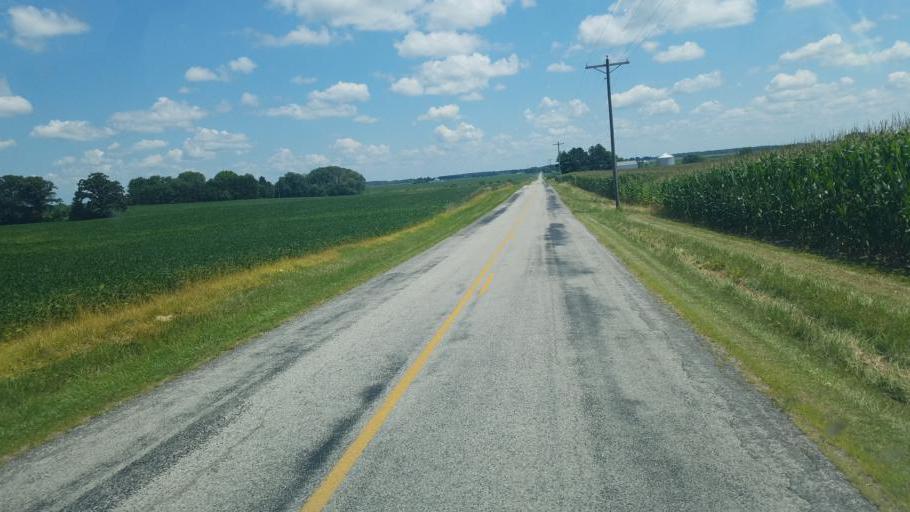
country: US
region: Ohio
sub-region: Marion County
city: Marion
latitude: 40.6587
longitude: -83.1685
